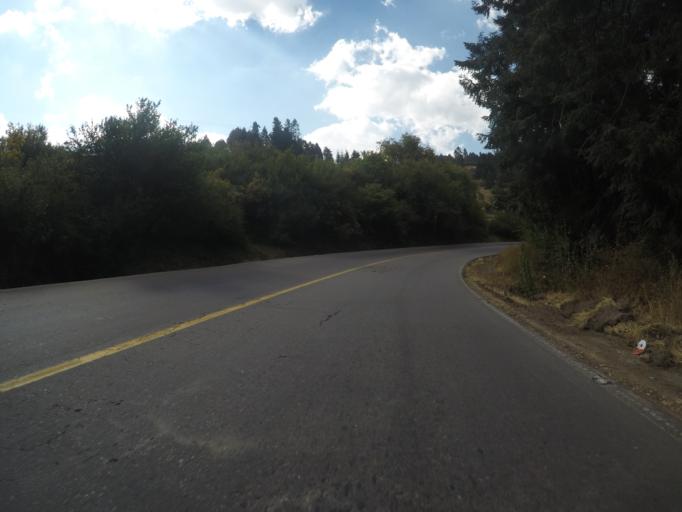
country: MX
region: Mexico
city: Cerro La Calera
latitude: 19.1765
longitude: -99.8043
